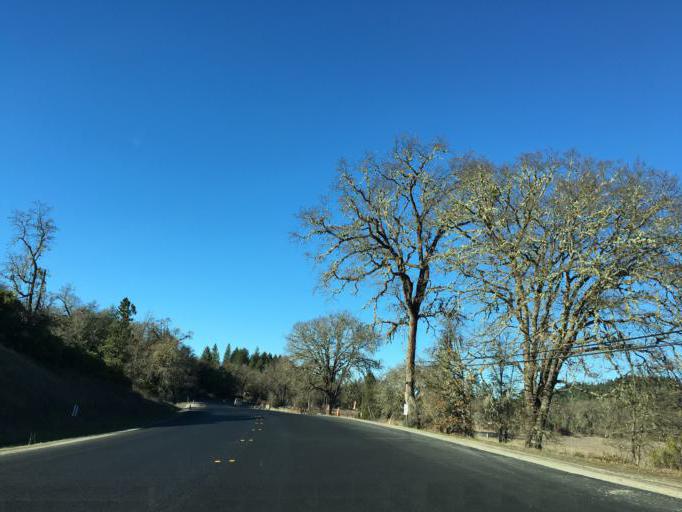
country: US
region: California
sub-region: Mendocino County
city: Laytonville
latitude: 39.6403
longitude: -123.4713
